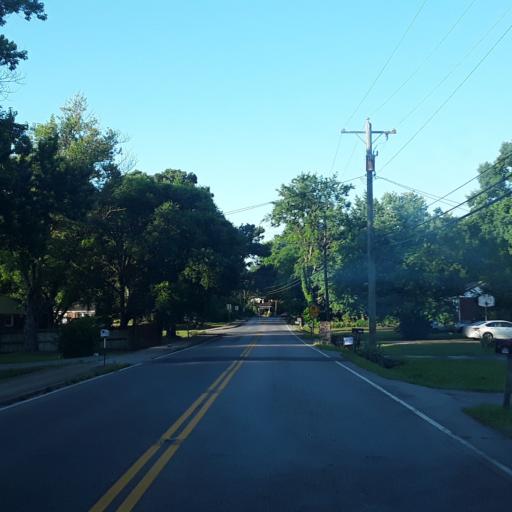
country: US
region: Tennessee
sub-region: Davidson County
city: Oak Hill
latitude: 36.1029
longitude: -86.7304
